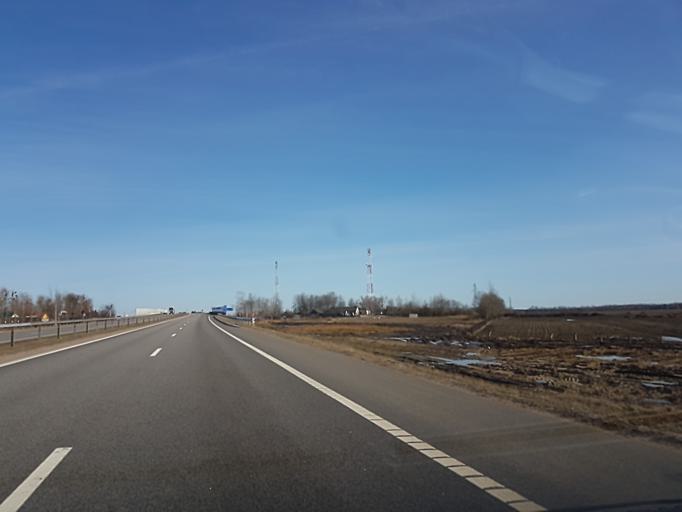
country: BY
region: Mogilev
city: Yalizava
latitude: 53.2502
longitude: 28.9253
